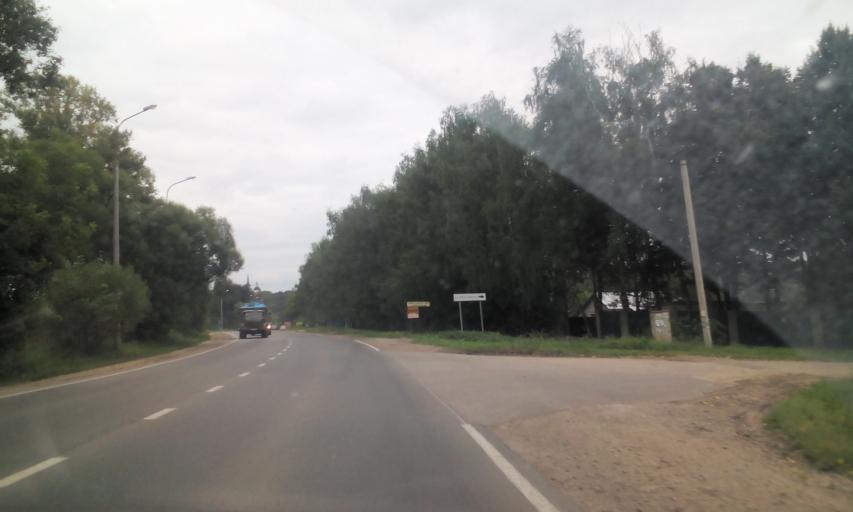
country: RU
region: Kaluga
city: Kaluga
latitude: 54.5141
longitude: 36.3621
